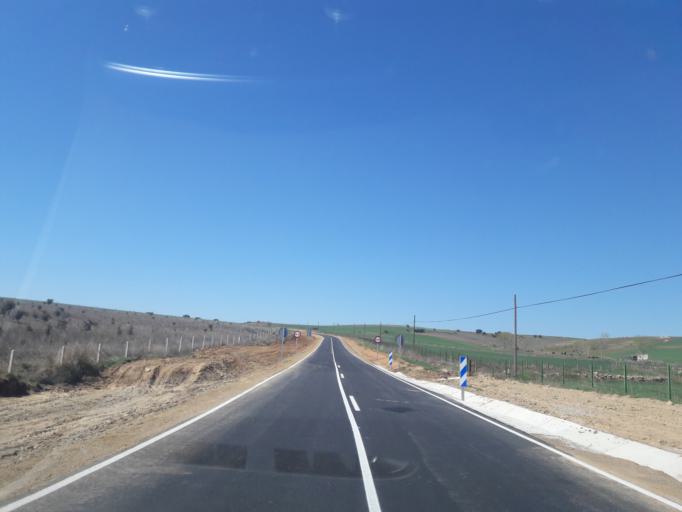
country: ES
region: Castille and Leon
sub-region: Provincia de Salamanca
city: Terradillos
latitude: 40.8267
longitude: -5.5475
